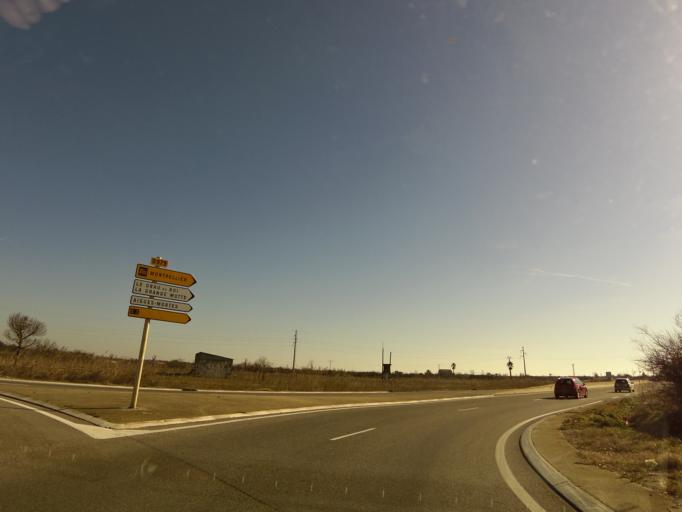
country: FR
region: Languedoc-Roussillon
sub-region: Departement du Gard
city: Aigues-Mortes
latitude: 43.6168
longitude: 4.1923
